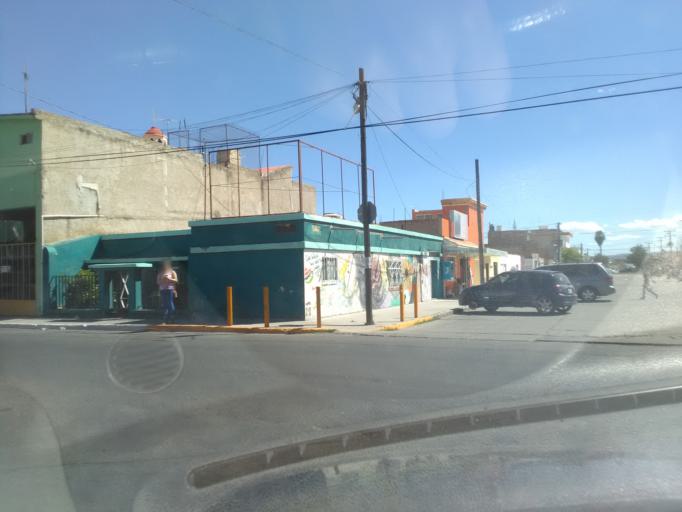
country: MX
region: Durango
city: Victoria de Durango
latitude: 24.0199
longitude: -104.6543
